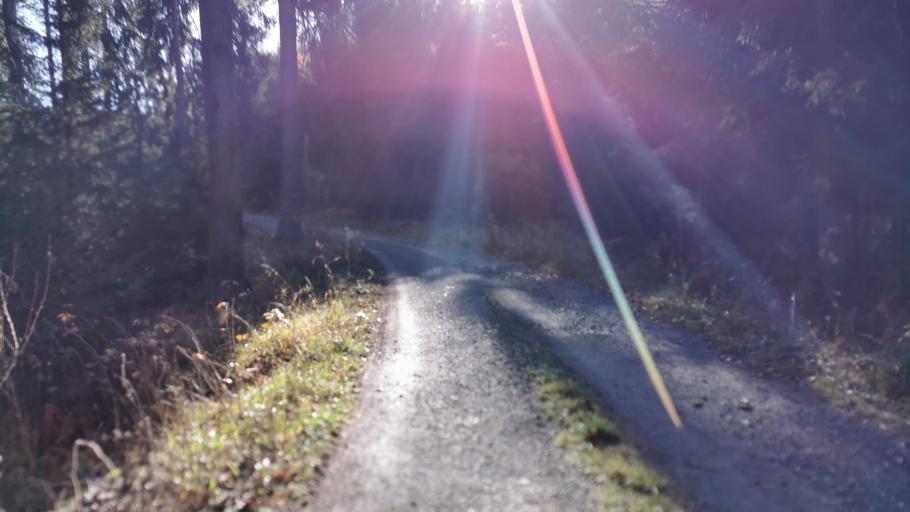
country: DE
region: Bavaria
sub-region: Upper Franconia
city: Reichenbach
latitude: 50.4512
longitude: 11.4343
